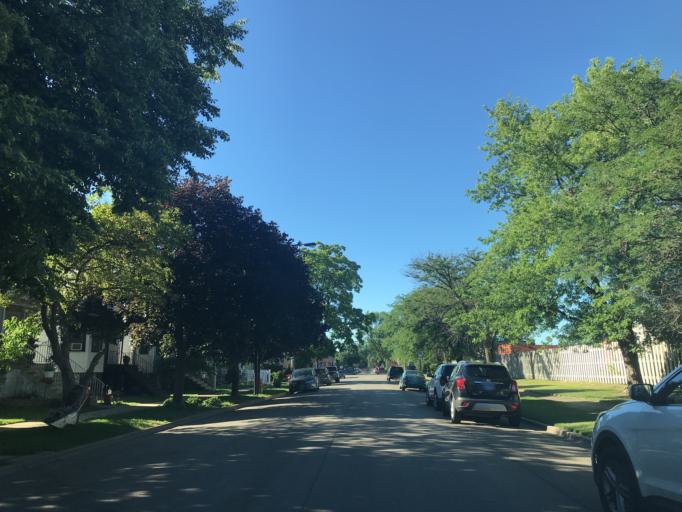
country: US
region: Illinois
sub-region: Cook County
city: Cicero
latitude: 41.8422
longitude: -87.7687
